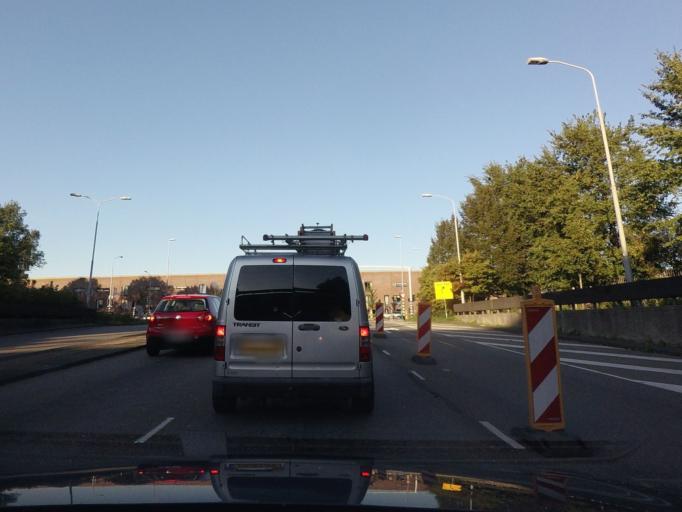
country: NL
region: North Holland
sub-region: Gemeente Haarlem
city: Haarlem
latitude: 52.3842
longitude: 4.6488
